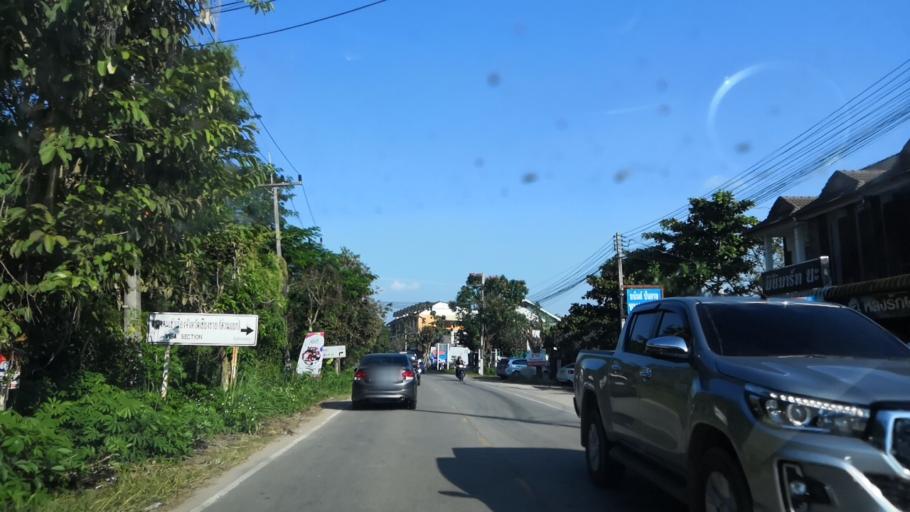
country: TH
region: Chiang Rai
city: Chiang Rai
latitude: 19.9297
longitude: 99.8606
